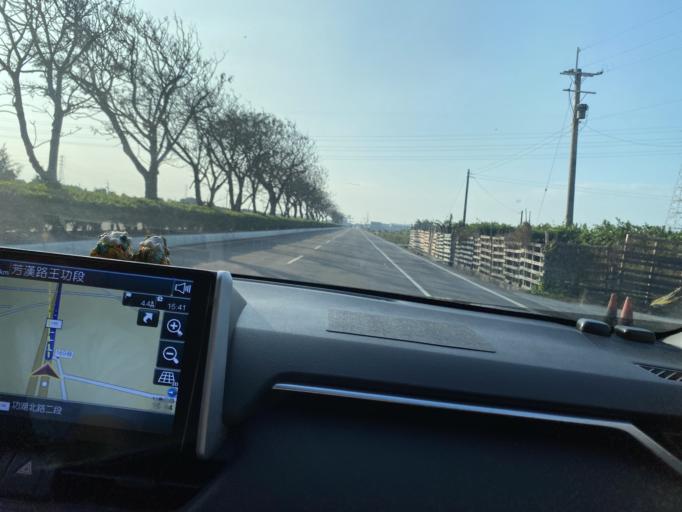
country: TW
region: Taiwan
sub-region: Changhua
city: Chang-hua
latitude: 23.9614
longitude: 120.3813
